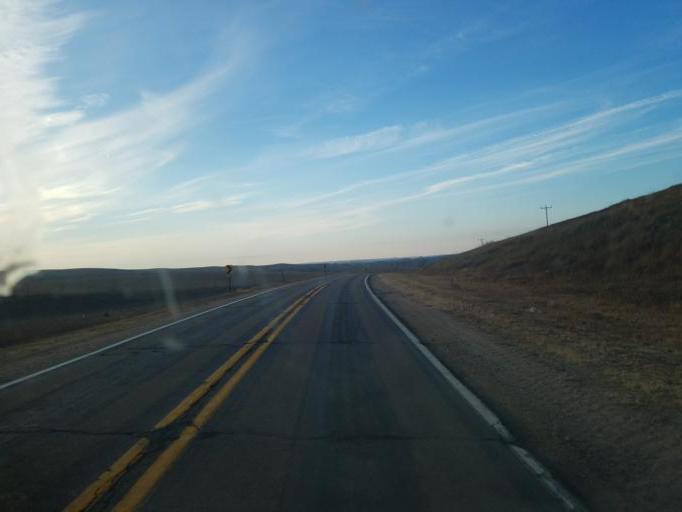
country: US
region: Nebraska
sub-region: Cedar County
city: Hartington
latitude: 42.7294
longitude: -97.1838
